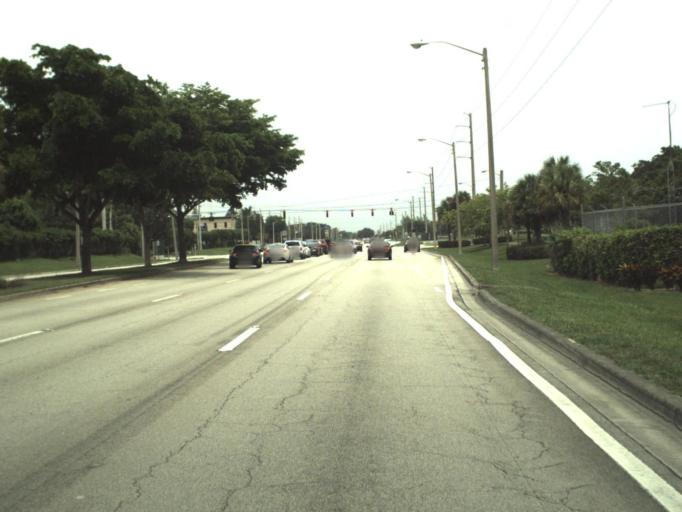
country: US
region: Florida
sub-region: Palm Beach County
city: Boca Del Mar
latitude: 26.3502
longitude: -80.1618
